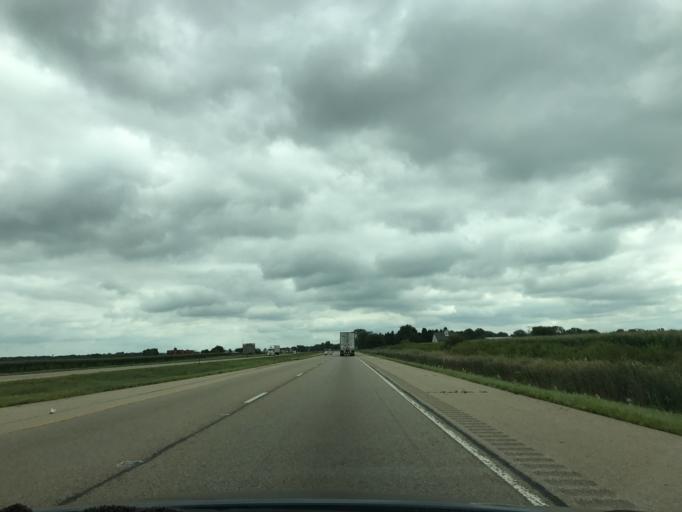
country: US
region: Illinois
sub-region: Bureau County
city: Ladd
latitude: 41.3655
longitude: -89.2070
